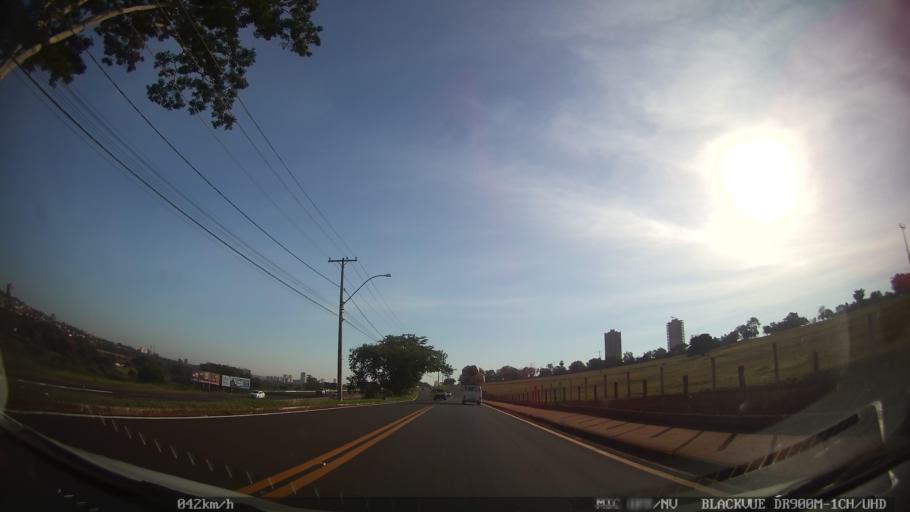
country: BR
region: Sao Paulo
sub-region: Ribeirao Preto
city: Ribeirao Preto
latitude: -21.2464
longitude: -47.8192
